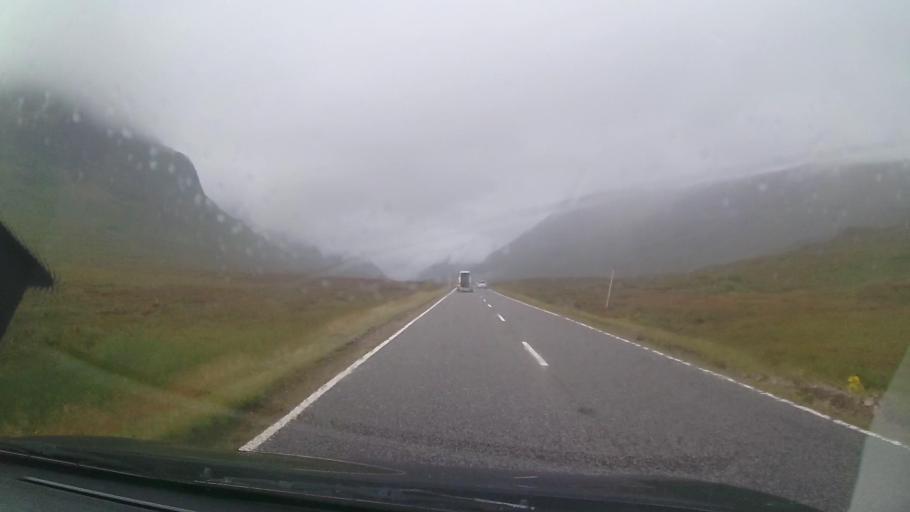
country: GB
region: Scotland
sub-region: Highland
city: Spean Bridge
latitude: 56.6621
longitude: -4.9248
